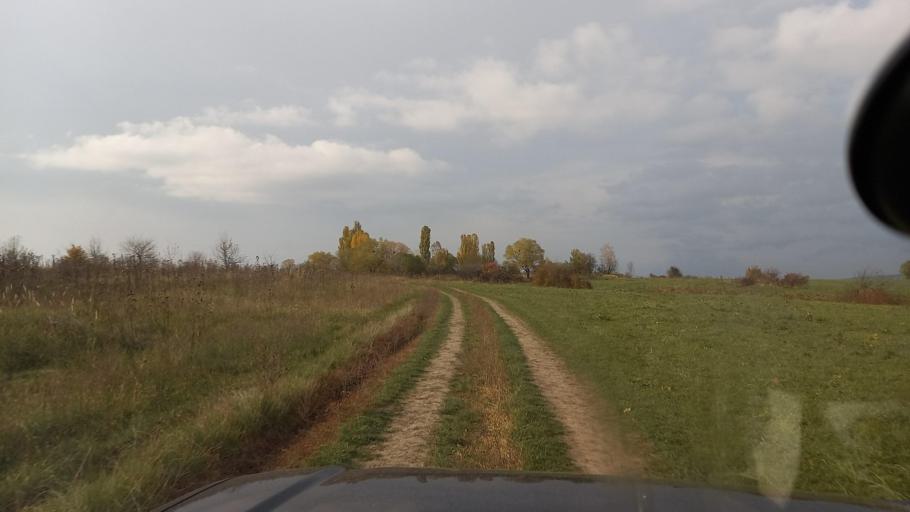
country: RU
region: Krasnodarskiy
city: Gubskaya
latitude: 44.3064
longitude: 40.5509
